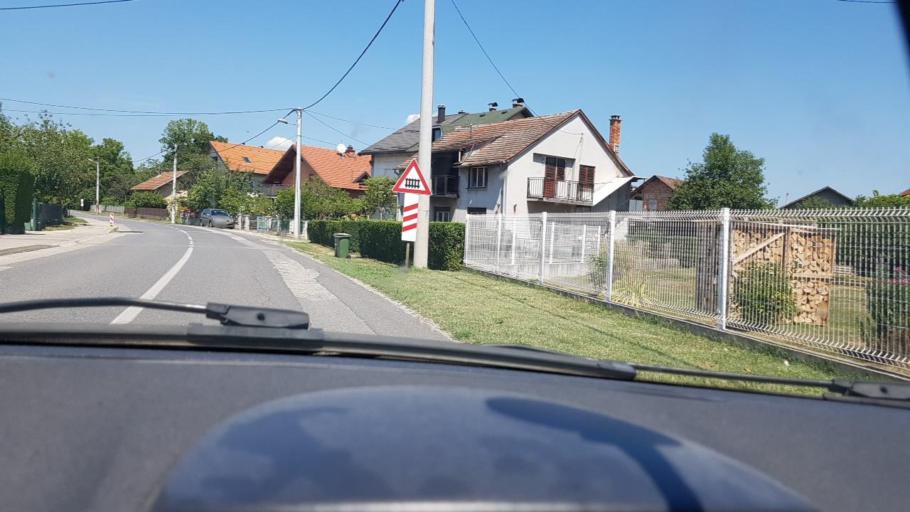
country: HR
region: Grad Zagreb
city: Brezovica
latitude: 45.7412
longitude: 15.8899
